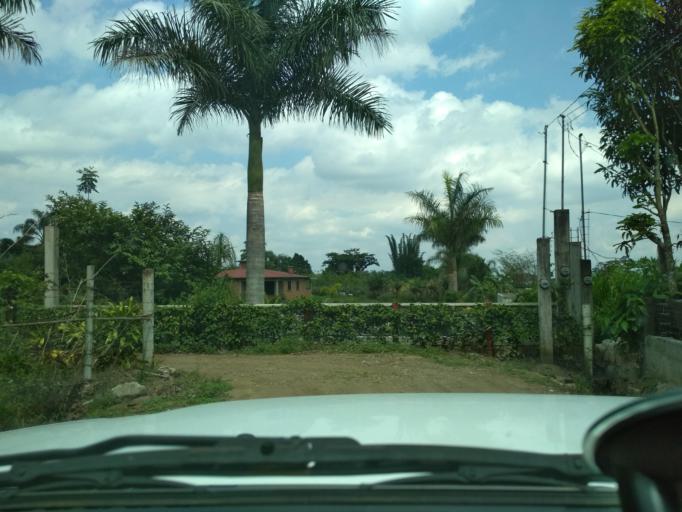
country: MX
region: Veracruz
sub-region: Fortin
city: Monte Salas
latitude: 18.9362
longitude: -97.0136
